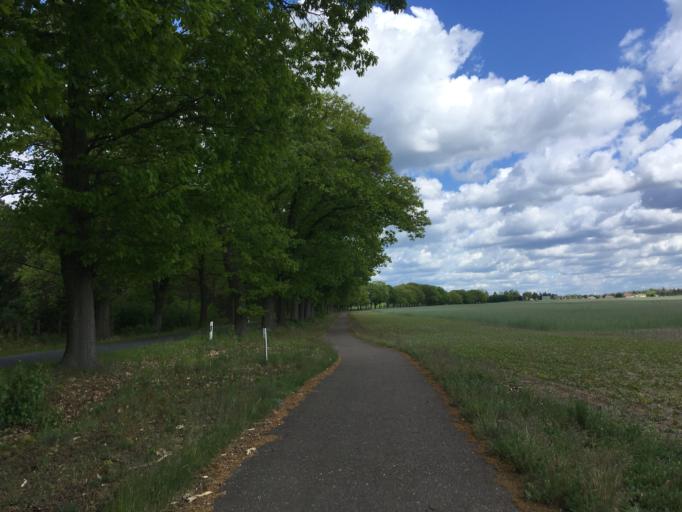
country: DE
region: Brandenburg
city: Marienwerder
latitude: 52.8989
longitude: 13.5104
